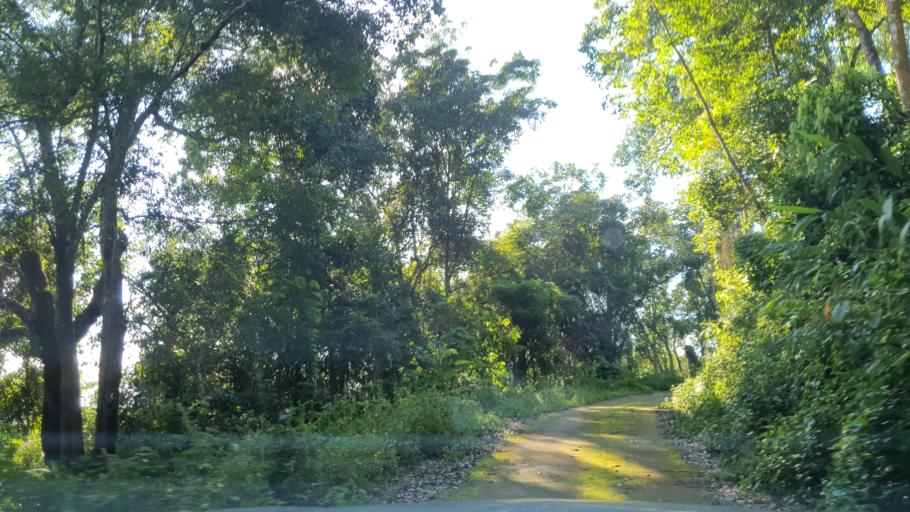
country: TH
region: Chiang Mai
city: Mae On
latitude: 18.8112
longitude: 99.3562
